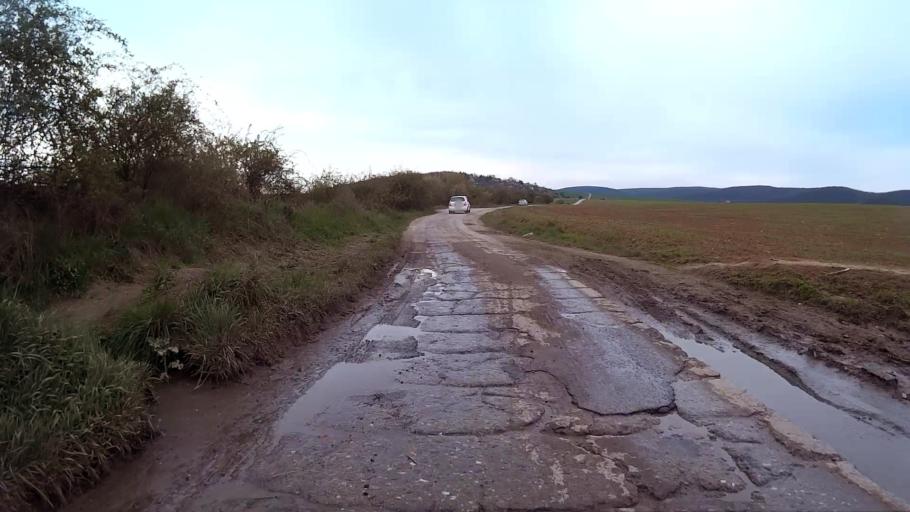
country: CZ
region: South Moravian
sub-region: Mesto Brno
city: Mokra Hora
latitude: 49.2346
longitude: 16.5470
